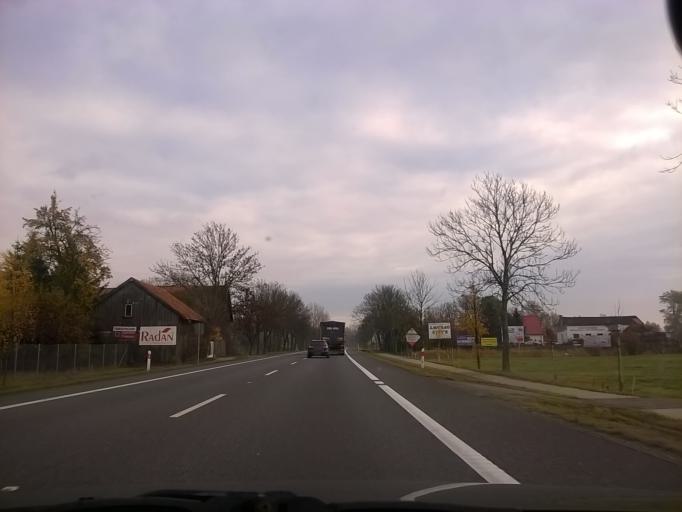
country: PL
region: Warmian-Masurian Voivodeship
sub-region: Powiat elblaski
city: Gronowo Elblaskie
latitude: 54.1672
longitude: 19.3003
